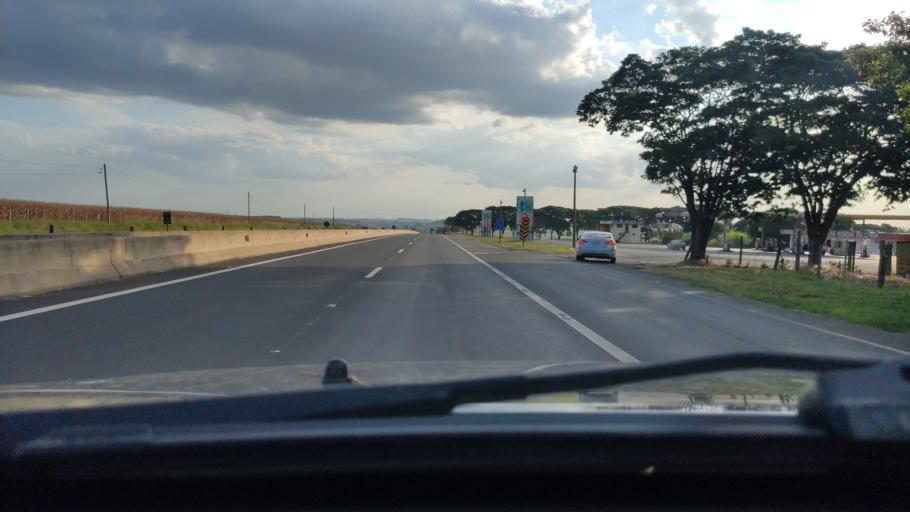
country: BR
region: Sao Paulo
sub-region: Artur Nogueira
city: Artur Nogueira
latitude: -22.4696
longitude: -47.1158
